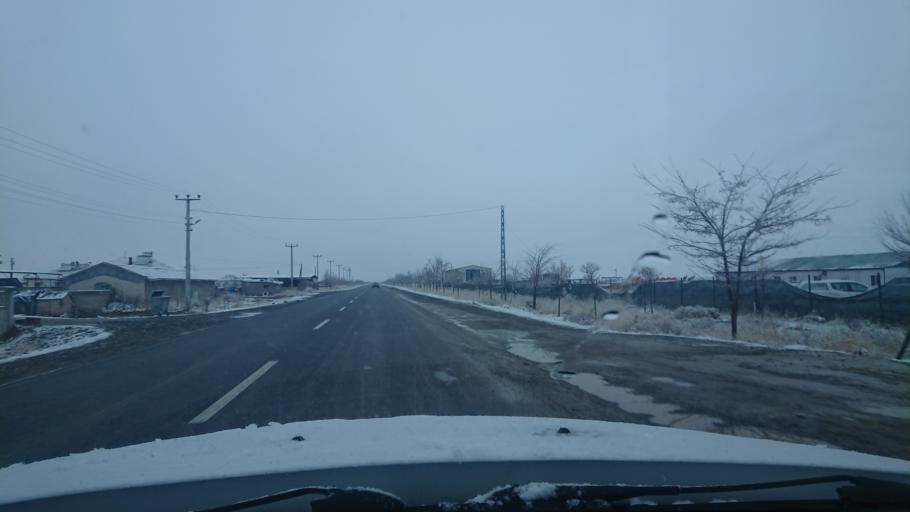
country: TR
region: Aksaray
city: Yesilova
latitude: 38.2970
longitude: 33.7584
